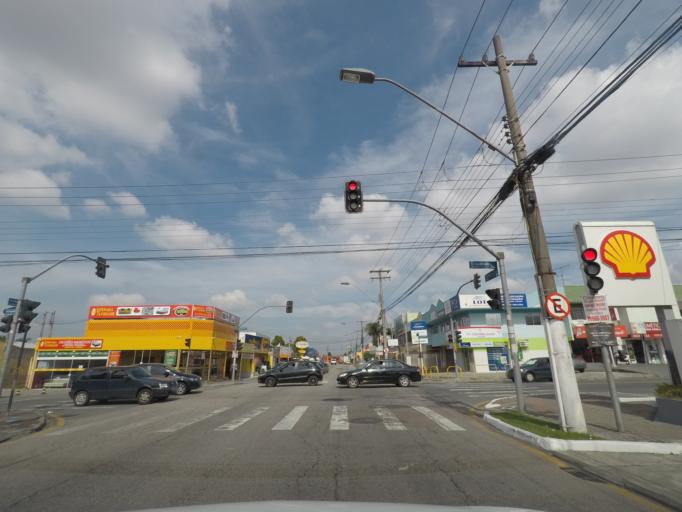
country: BR
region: Parana
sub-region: Pinhais
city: Pinhais
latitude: -25.4678
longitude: -49.2090
